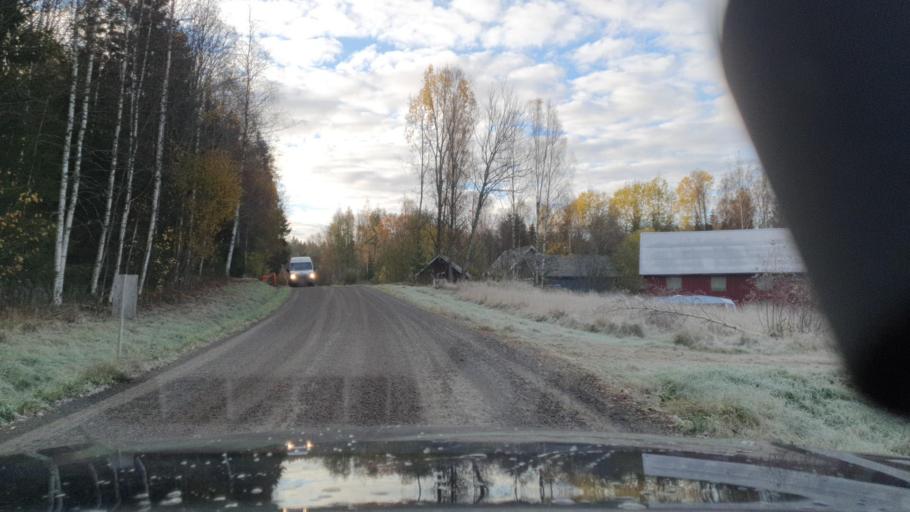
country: SE
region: Vaermland
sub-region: Eda Kommun
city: Amotfors
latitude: 59.7824
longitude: 12.3415
